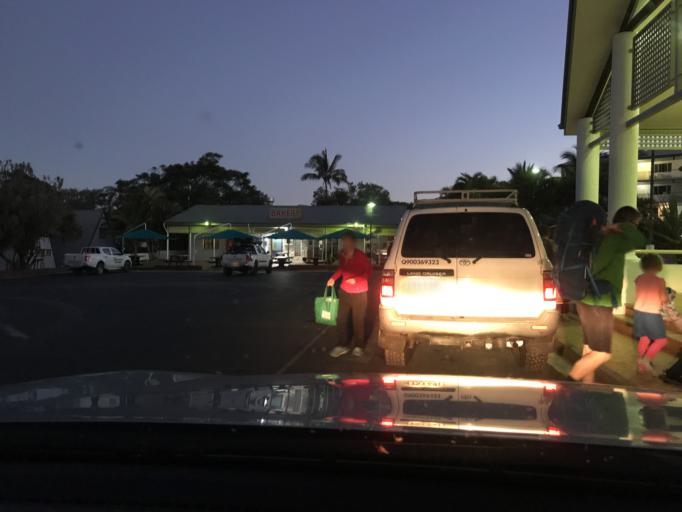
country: AU
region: Queensland
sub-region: Fraser Coast
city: Urangan
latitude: -25.5093
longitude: 153.1259
